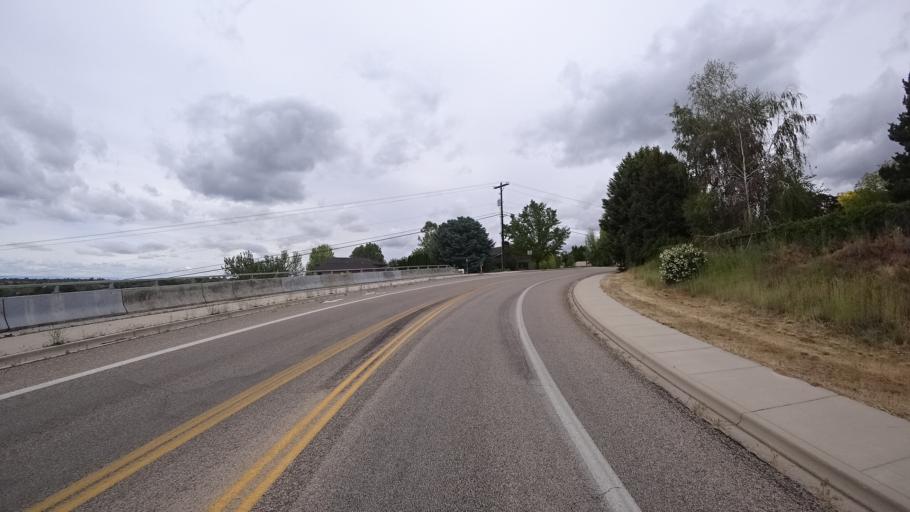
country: US
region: Idaho
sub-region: Ada County
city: Eagle
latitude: 43.6970
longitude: -116.3333
